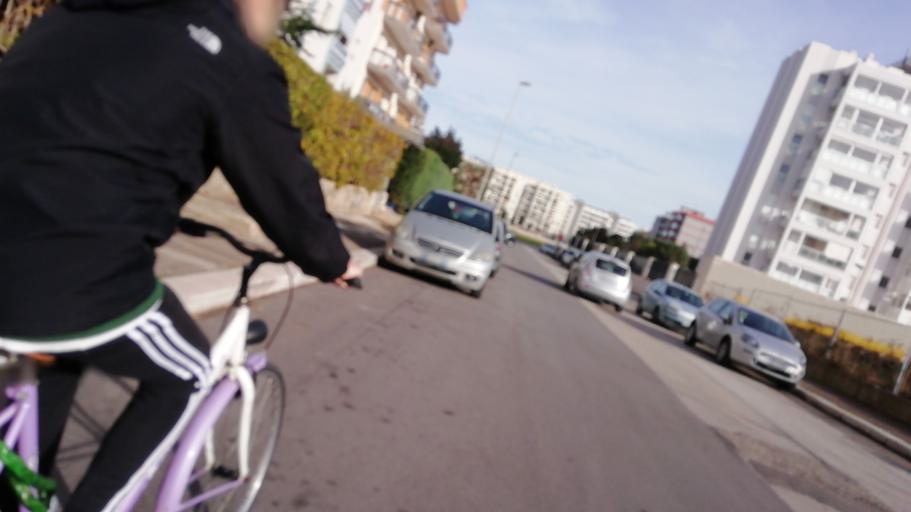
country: IT
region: Apulia
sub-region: Provincia di Bari
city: Triggiano
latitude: 41.1022
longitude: 16.9141
